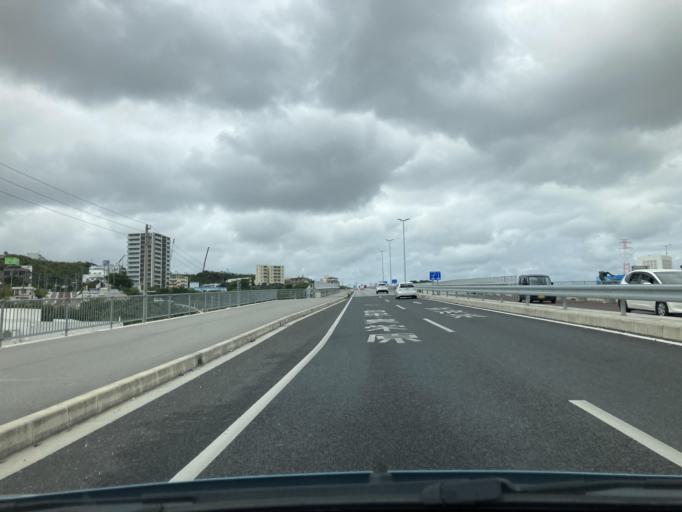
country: JP
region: Okinawa
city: Ginowan
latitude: 26.2407
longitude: 127.7444
